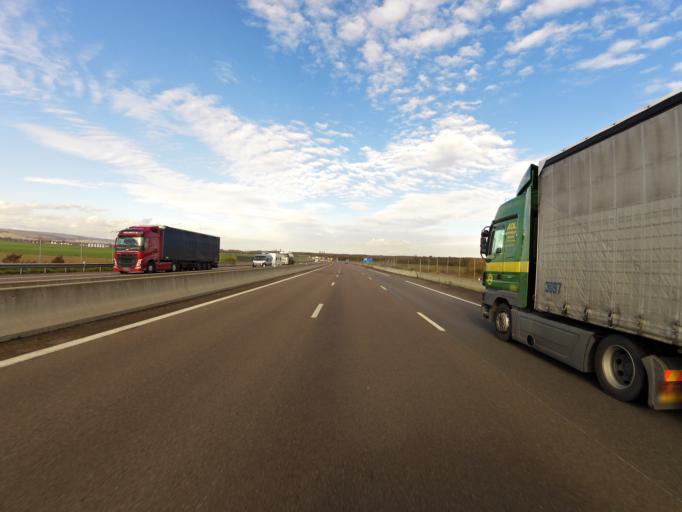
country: FR
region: Bourgogne
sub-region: Departement de la Cote-d'Or
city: Nuits-Saint-Georges
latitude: 47.1535
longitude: 4.9952
